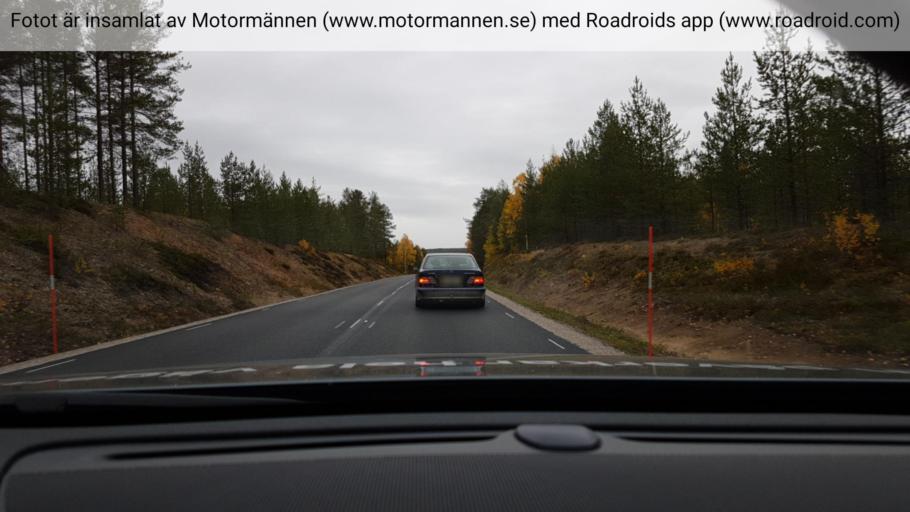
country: SE
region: Norrbotten
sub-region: Overkalix Kommun
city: OEverkalix
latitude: 66.4461
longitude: 22.7862
